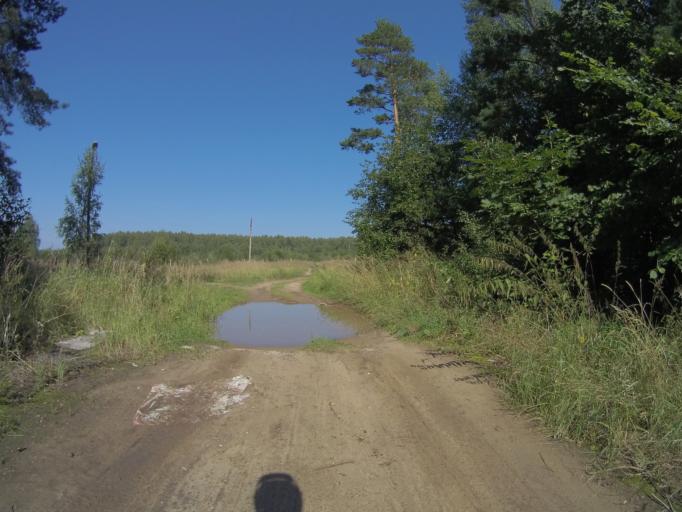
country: RU
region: Vladimir
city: Orgtrud
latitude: 56.2516
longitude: 40.5786
